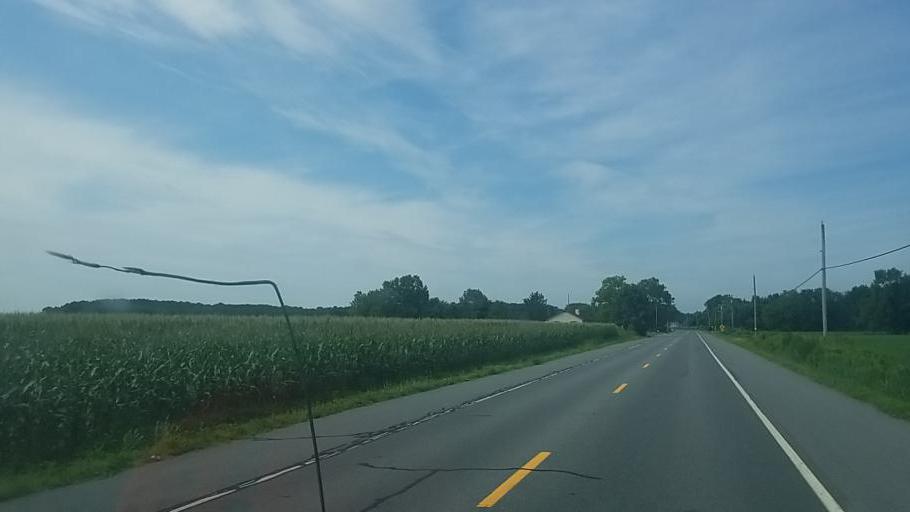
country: US
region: Delaware
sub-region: Sussex County
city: Selbyville
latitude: 38.5352
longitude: -75.1878
